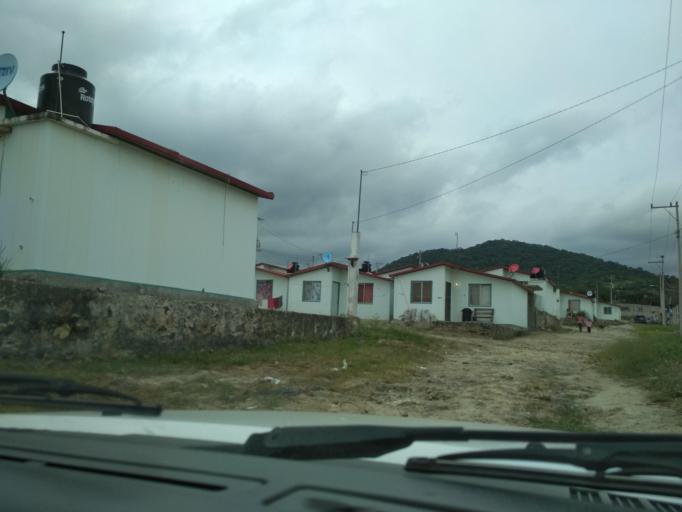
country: MX
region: Veracruz
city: El Castillo
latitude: 19.5849
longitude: -96.8284
